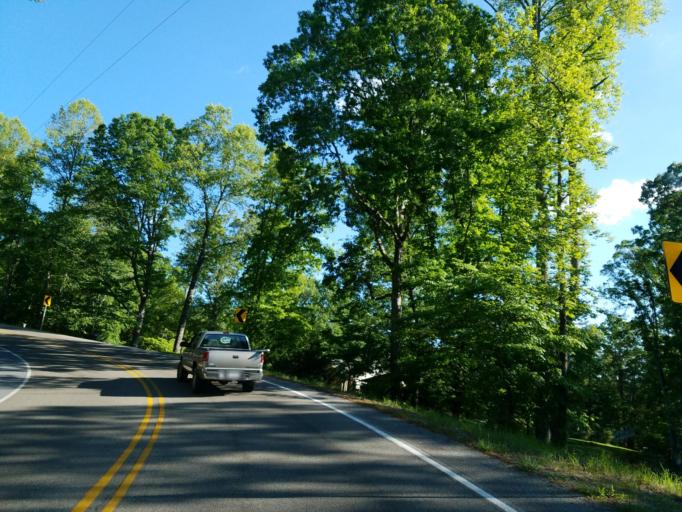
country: US
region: Georgia
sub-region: Fannin County
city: Blue Ridge
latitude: 34.8579
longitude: -84.2296
